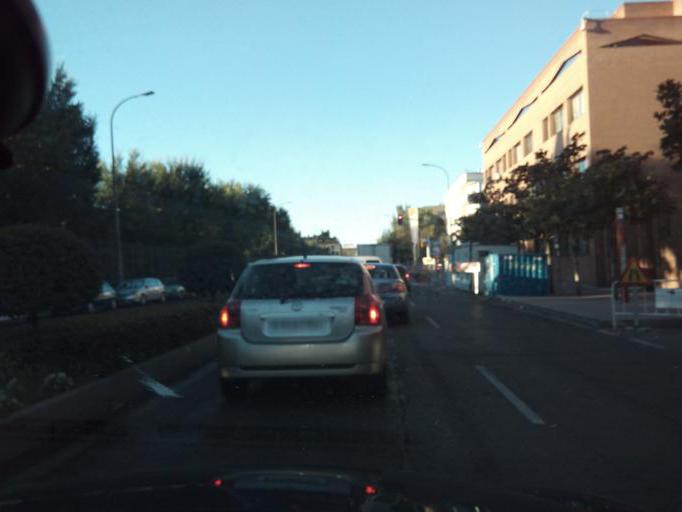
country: ES
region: Madrid
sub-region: Provincia de Madrid
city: Torrejon de Ardoz
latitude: 40.4588
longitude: -3.4835
